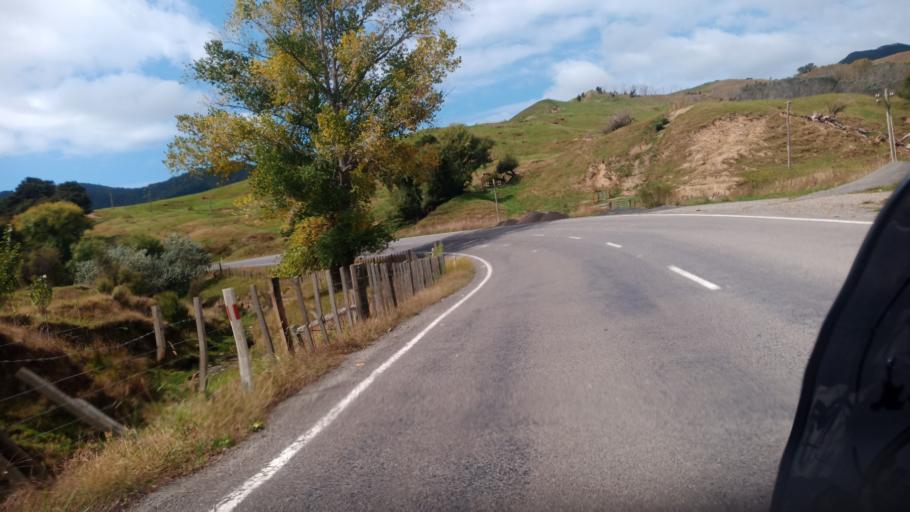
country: NZ
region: Gisborne
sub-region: Gisborne District
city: Gisborne
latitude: -38.1626
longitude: 178.2679
